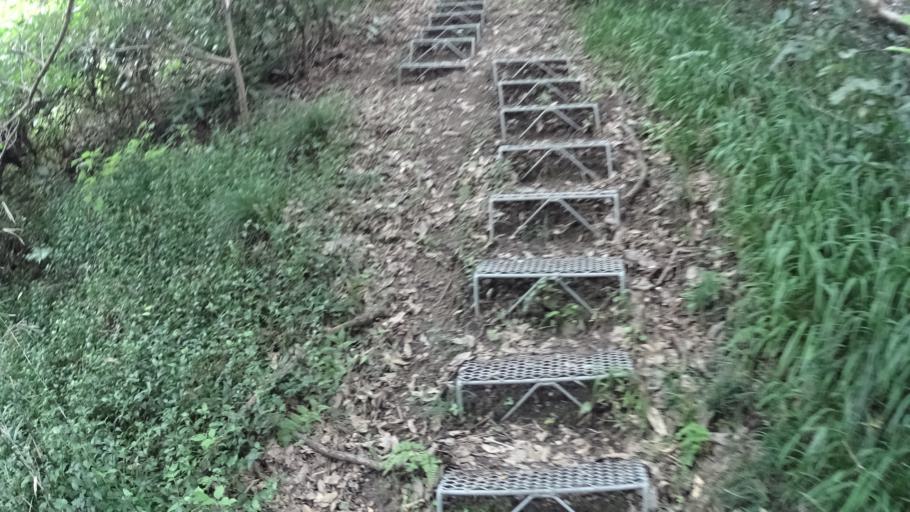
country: JP
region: Kanagawa
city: Zushi
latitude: 35.2983
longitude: 139.6195
